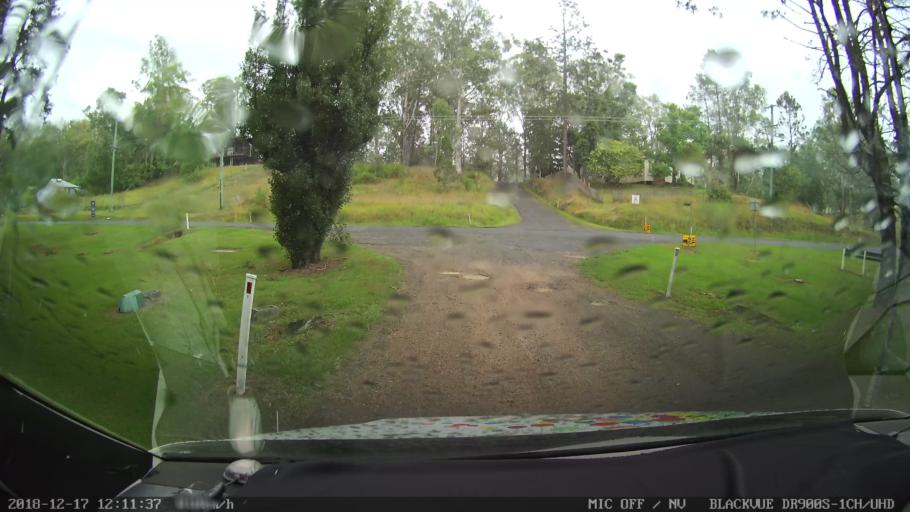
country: AU
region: New South Wales
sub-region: Kyogle
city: Kyogle
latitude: -28.4683
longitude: 152.5486
